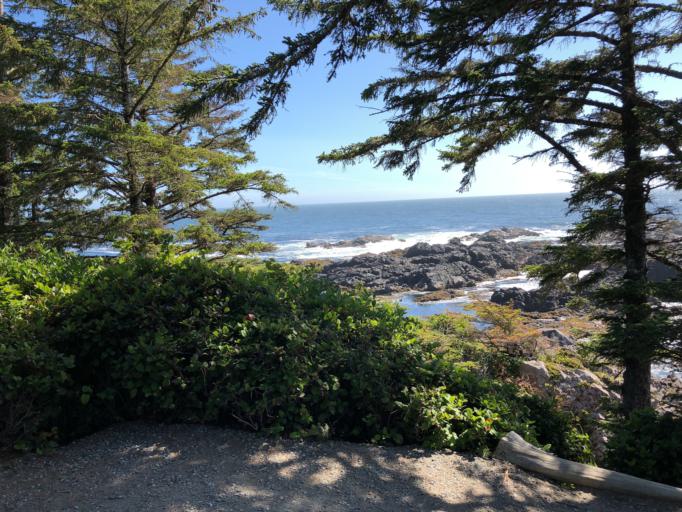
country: CA
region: British Columbia
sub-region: Regional District of Alberni-Clayoquot
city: Ucluelet
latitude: 48.9221
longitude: -125.5430
